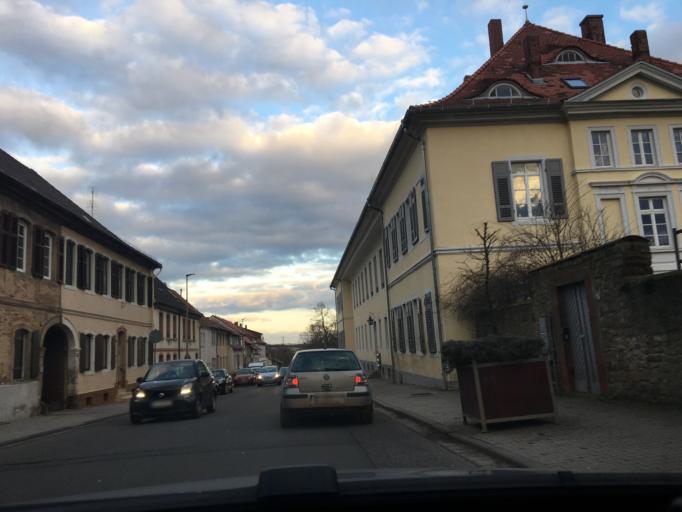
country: DE
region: Rheinland-Pfalz
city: Kirchheimbolanden
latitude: 49.6682
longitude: 8.0090
